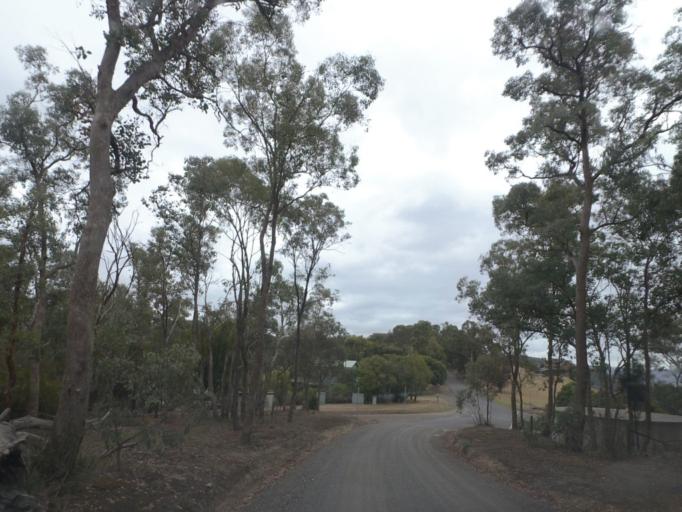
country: AU
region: Victoria
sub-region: Yarra Ranges
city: Yarra Glen
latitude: -37.6427
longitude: 145.3536
